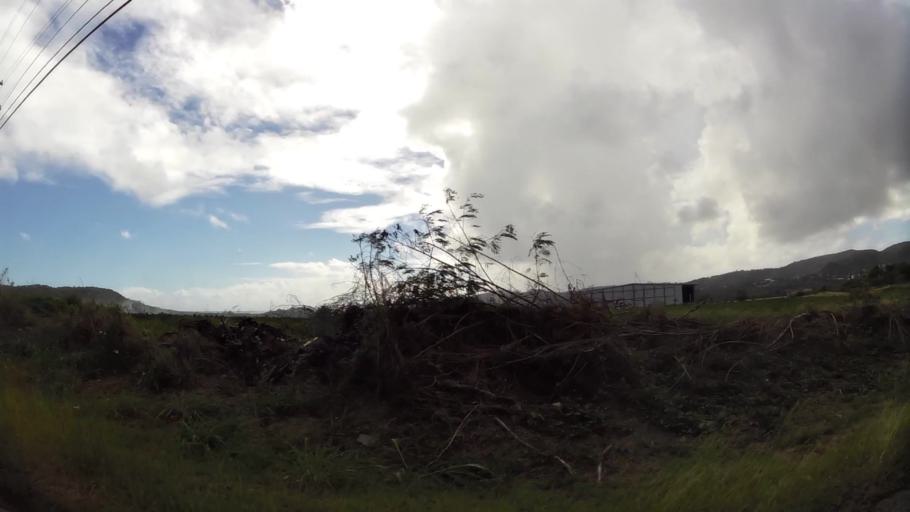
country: AG
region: Saint Paul
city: Liberta
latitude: 17.0539
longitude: -61.7456
